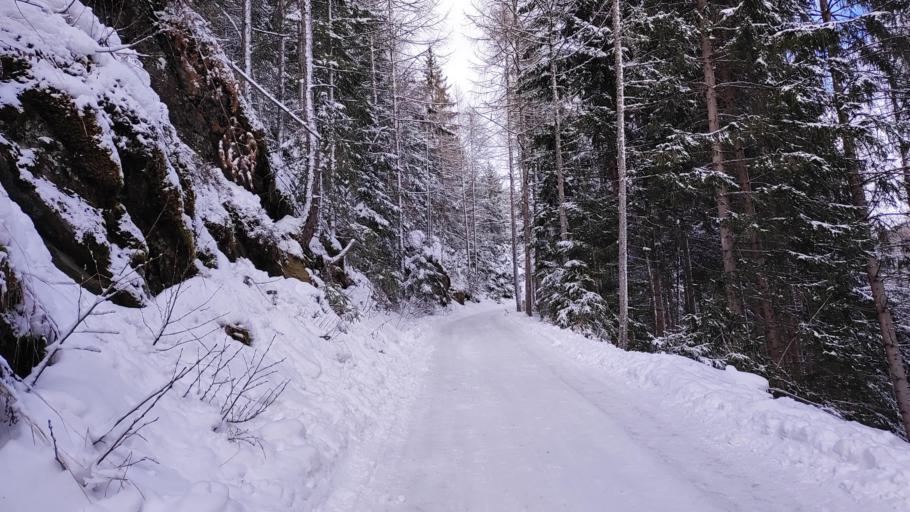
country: AT
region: Tyrol
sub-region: Politischer Bezirk Imst
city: Umhausen
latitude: 47.0987
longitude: 10.9367
